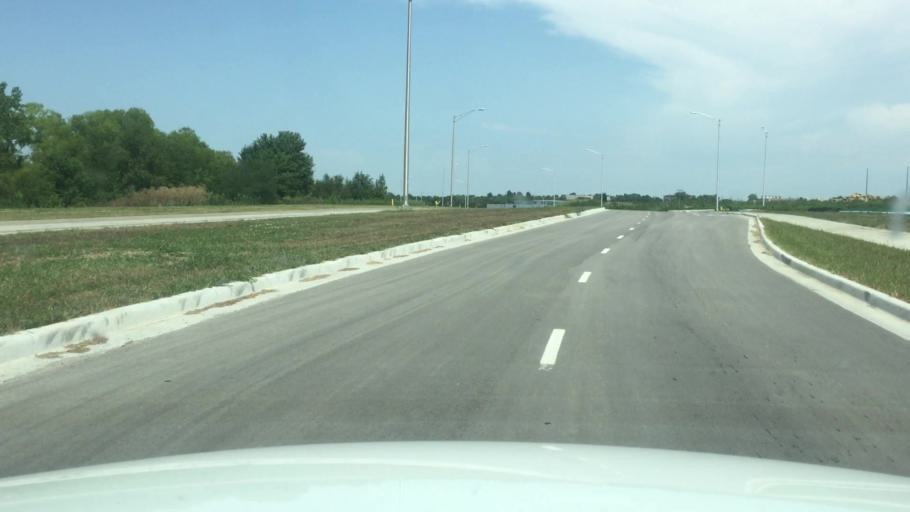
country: US
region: Missouri
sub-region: Jackson County
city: Lees Summit
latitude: 38.9270
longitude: -94.3936
